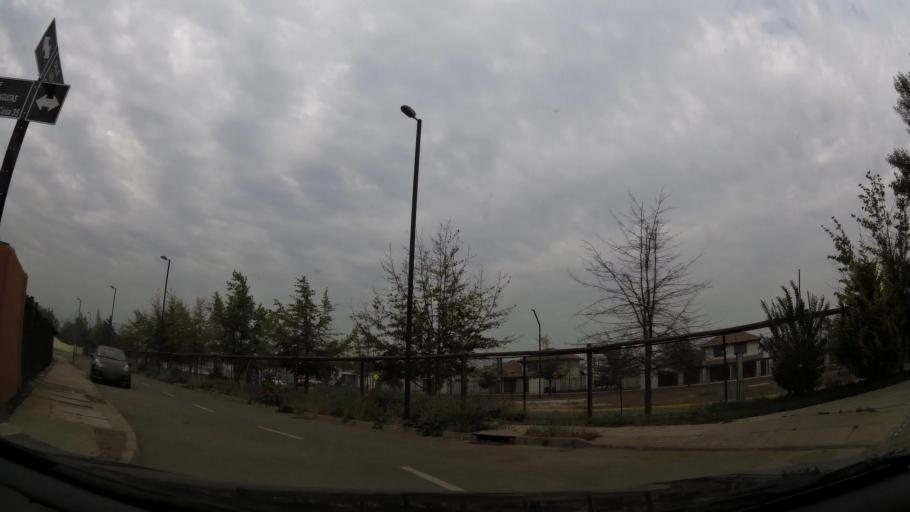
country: CL
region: Santiago Metropolitan
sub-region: Provincia de Chacabuco
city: Chicureo Abajo
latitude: -33.2168
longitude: -70.6689
